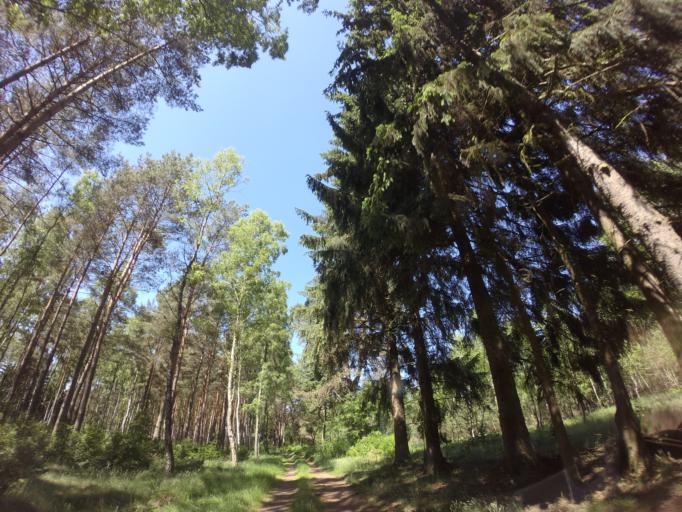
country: PL
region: West Pomeranian Voivodeship
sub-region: Powiat walecki
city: Miroslawiec
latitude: 53.2333
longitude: 16.0238
